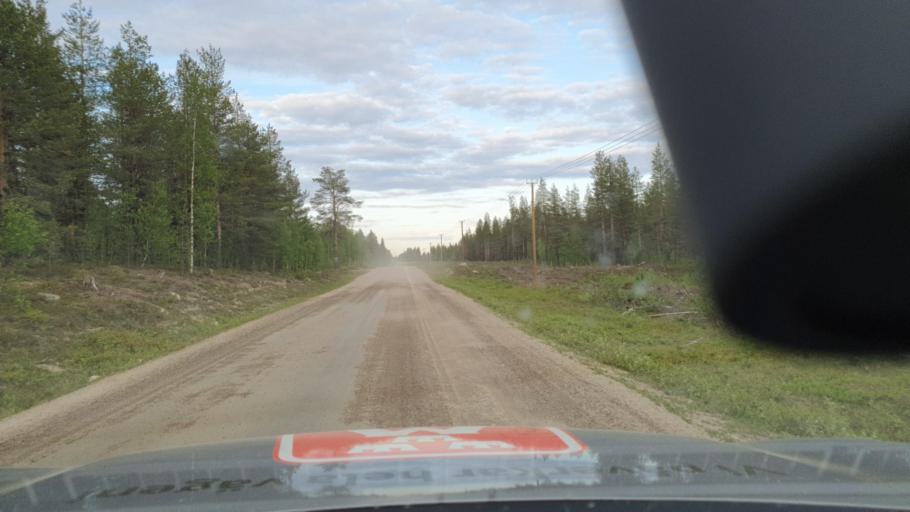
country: SE
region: Norrbotten
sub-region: Gallivare Kommun
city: Gaellivare
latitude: 66.7420
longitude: 21.1219
